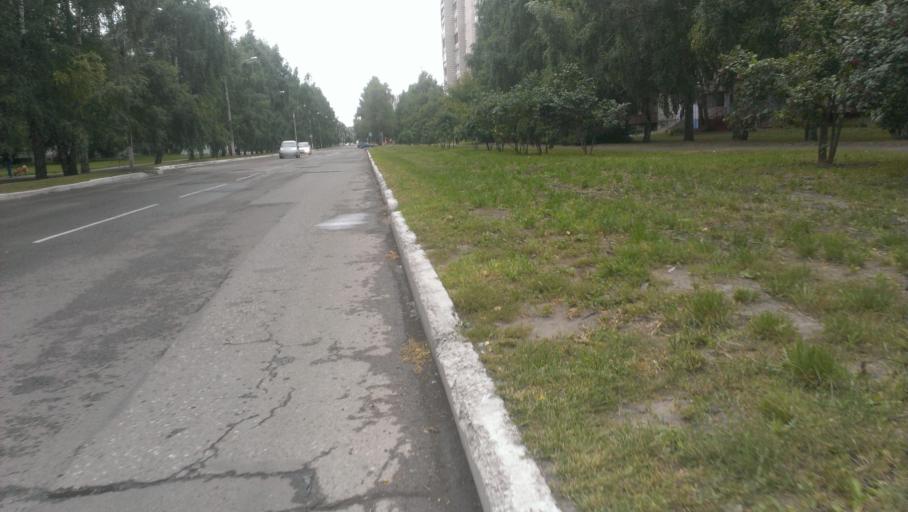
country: RU
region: Altai Krai
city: Novosilikatnyy
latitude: 53.3709
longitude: 83.6694
